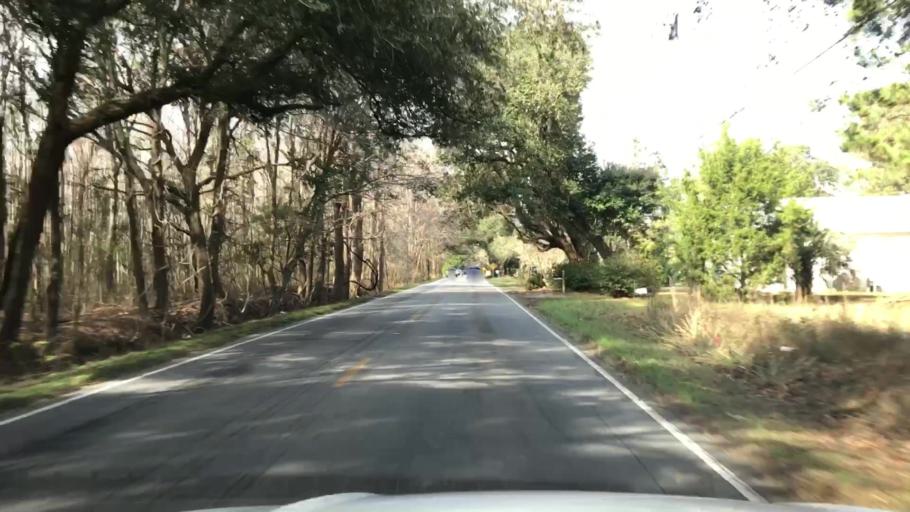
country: US
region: South Carolina
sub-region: Charleston County
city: Shell Point
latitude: 32.7616
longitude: -80.0585
